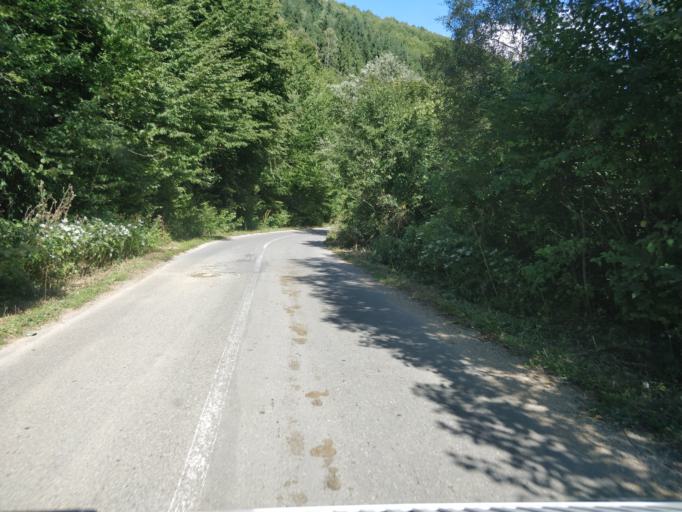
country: RO
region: Cluj
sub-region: Comuna Sacueu
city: Sacuieu
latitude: 46.8505
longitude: 22.8619
